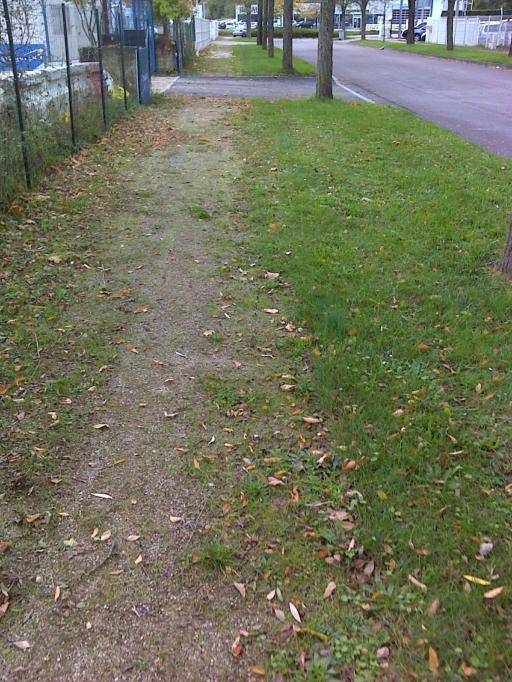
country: FR
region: Bourgogne
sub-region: Departement de la Cote-d'Or
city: Ruffey-les-Echirey
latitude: 47.3543
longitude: 5.0662
